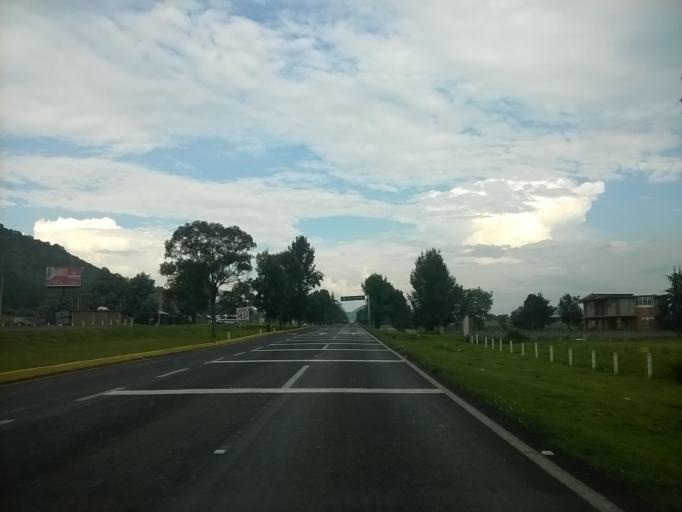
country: MX
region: Michoacan
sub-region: Huiramba
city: El Pedregal
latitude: 19.5317
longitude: -101.4893
